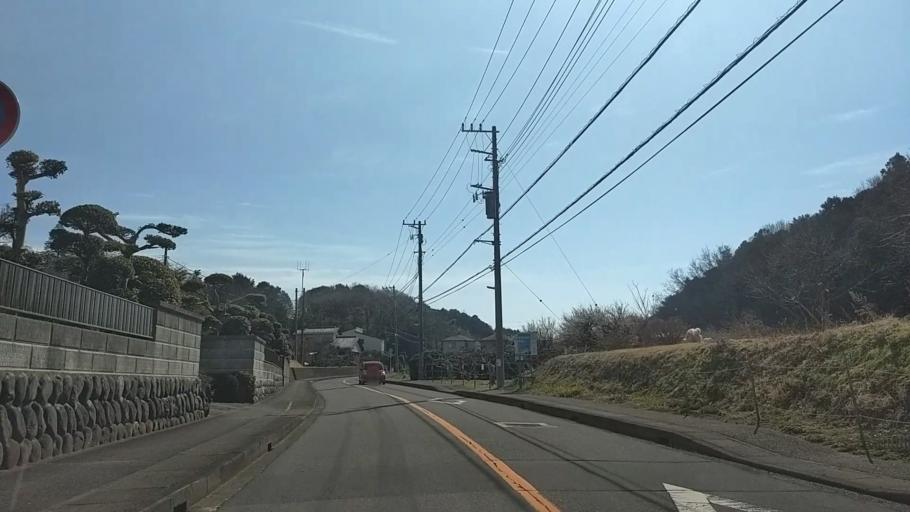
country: JP
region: Kanagawa
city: Fujisawa
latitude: 35.3771
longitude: 139.4284
